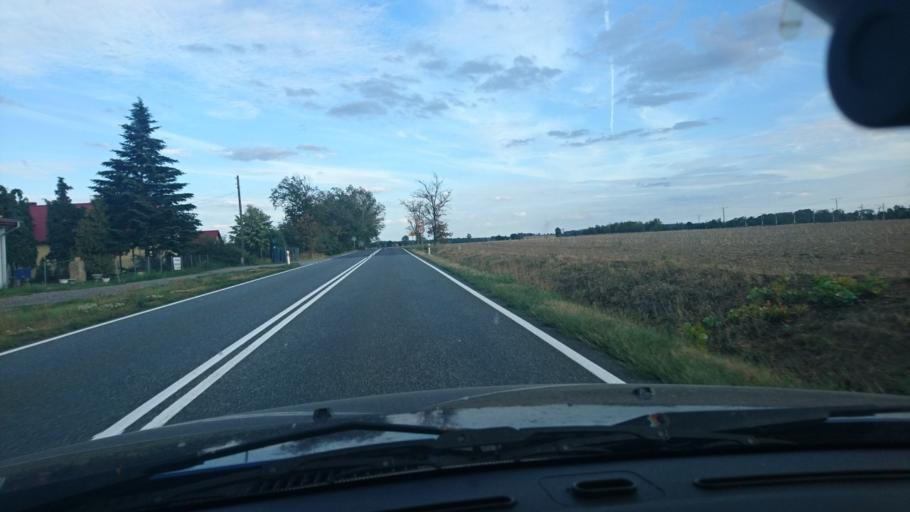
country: PL
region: Lodz Voivodeship
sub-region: Powiat wieruszowski
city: Boleslawiec
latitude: 51.1587
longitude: 18.1660
